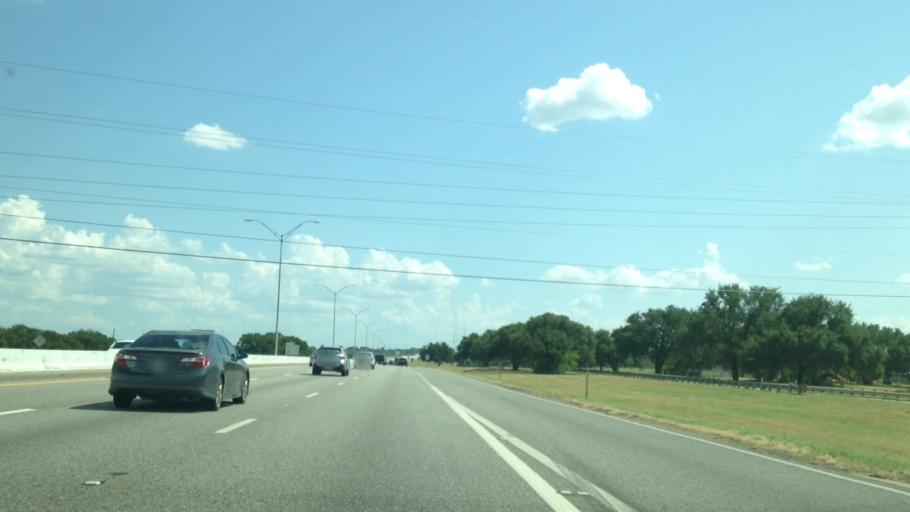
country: US
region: Texas
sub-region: Williamson County
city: Georgetown
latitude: 30.6180
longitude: -97.6890
